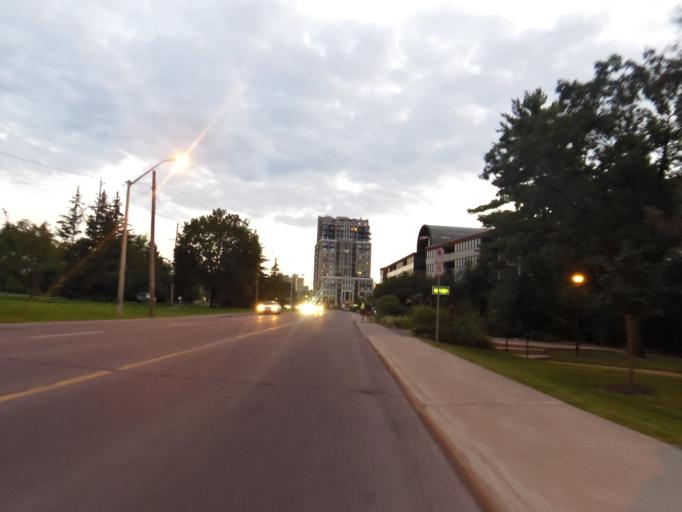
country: CA
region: Ontario
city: Ottawa
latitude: 45.3838
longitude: -75.7681
